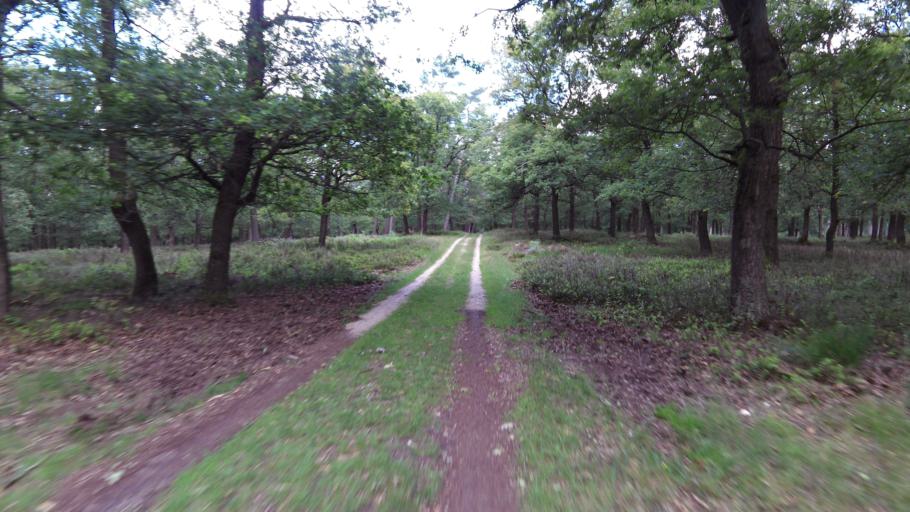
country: NL
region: Gelderland
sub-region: Gemeente Apeldoorn
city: Uddel
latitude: 52.2388
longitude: 5.8234
